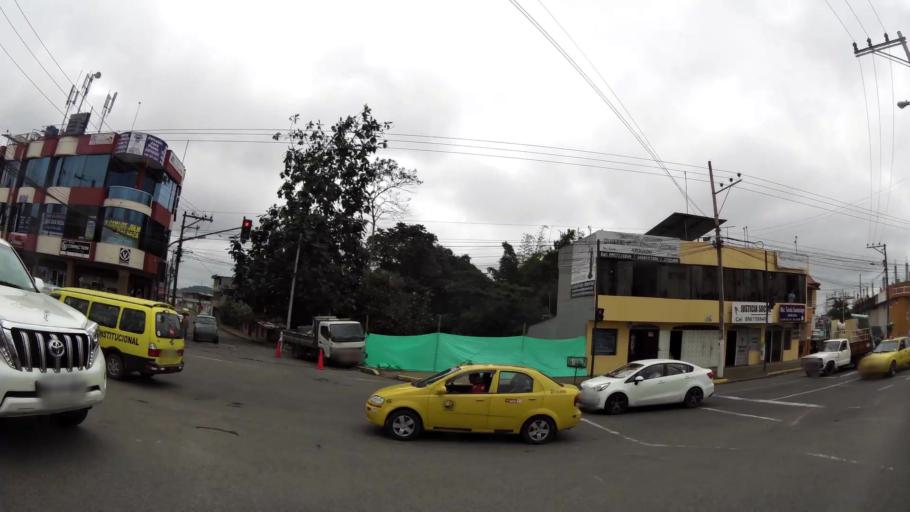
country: EC
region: Santo Domingo de los Tsachilas
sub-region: Canton Santo Domingo de los Colorados
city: Santo Domingo de los Colorados
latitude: -0.2637
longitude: -79.1686
